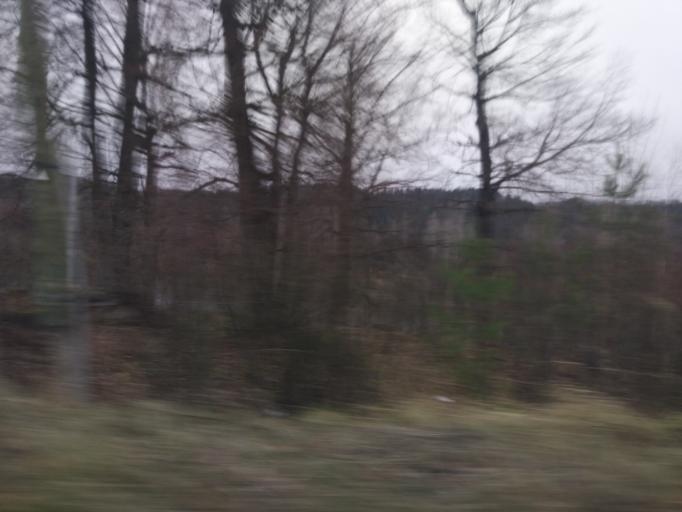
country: RU
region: Kirov
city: Krasnaya Polyana
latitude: 56.2437
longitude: 51.1756
